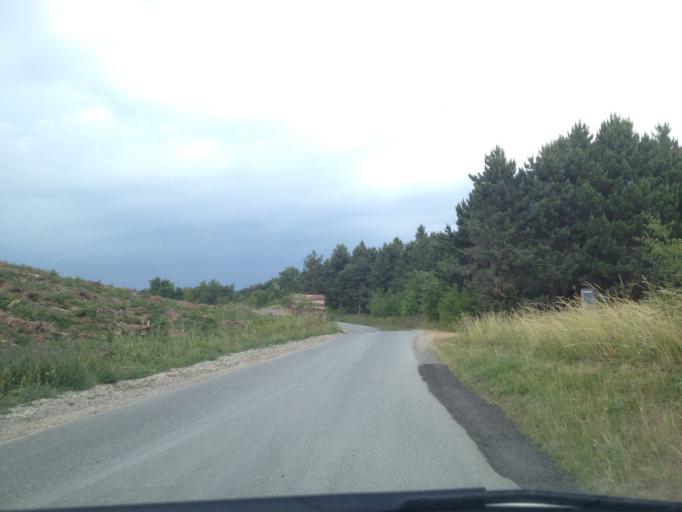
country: DK
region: Central Jutland
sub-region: Syddjurs Kommune
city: Ebeltoft
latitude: 56.1616
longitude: 10.6868
